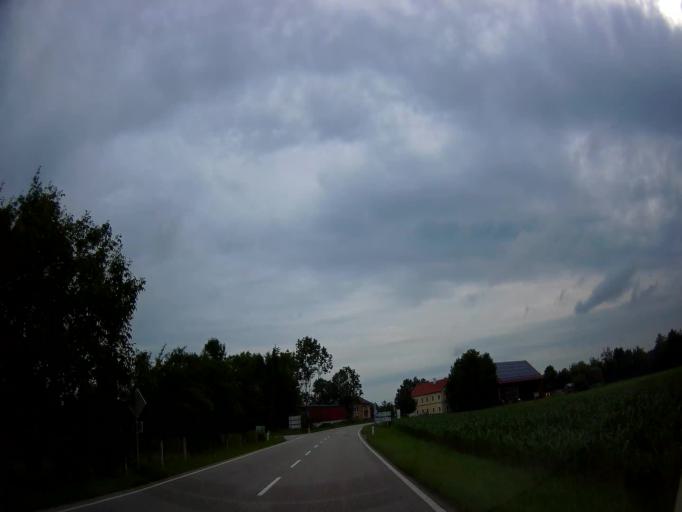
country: AT
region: Upper Austria
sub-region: Politischer Bezirk Braunau am Inn
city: Altheim
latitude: 48.2203
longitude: 13.1650
